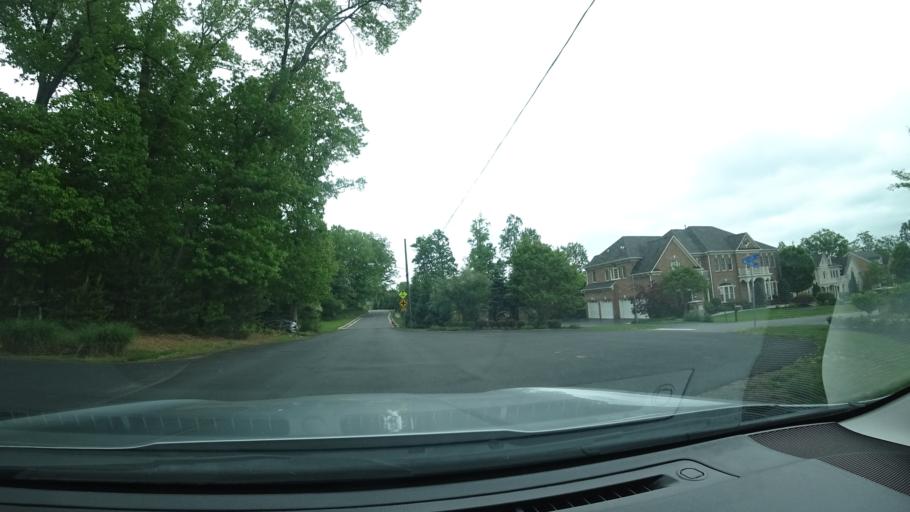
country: US
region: Virginia
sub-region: City of Fairfax
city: Fairfax
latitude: 38.8664
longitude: -77.3395
